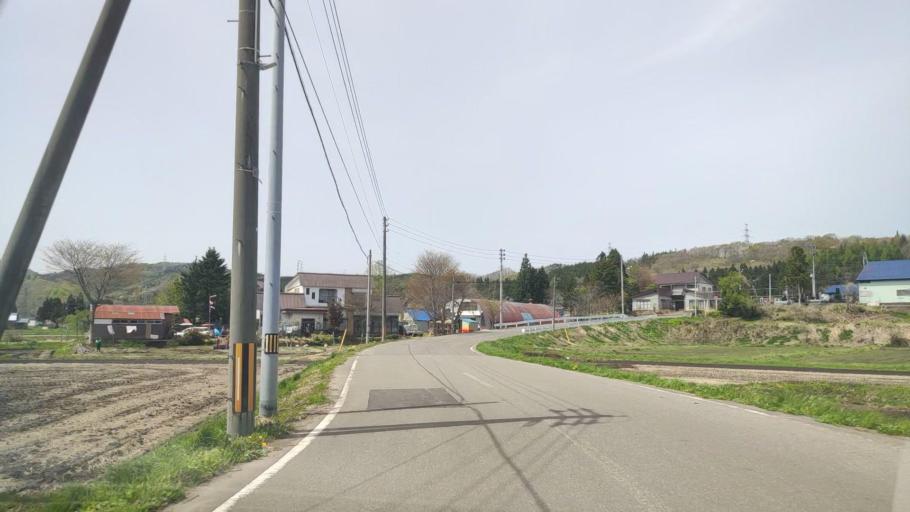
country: JP
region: Aomori
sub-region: Misawa Shi
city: Inuotose
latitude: 40.7877
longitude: 141.1100
